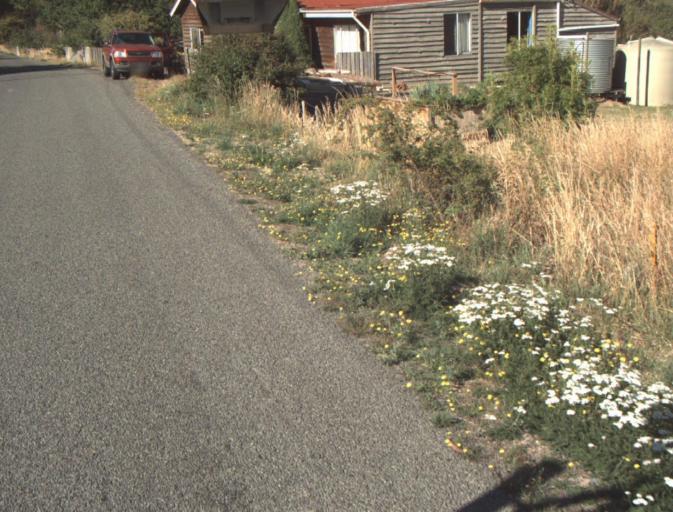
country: AU
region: Tasmania
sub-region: Launceston
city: Newstead
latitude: -41.3543
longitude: 147.3035
